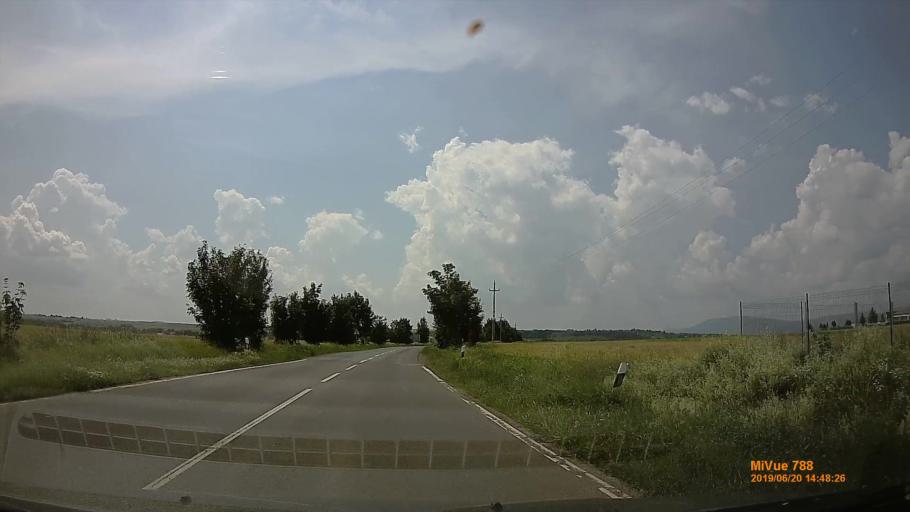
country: HU
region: Baranya
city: Kozarmisleny
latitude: 46.0152
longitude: 18.2886
